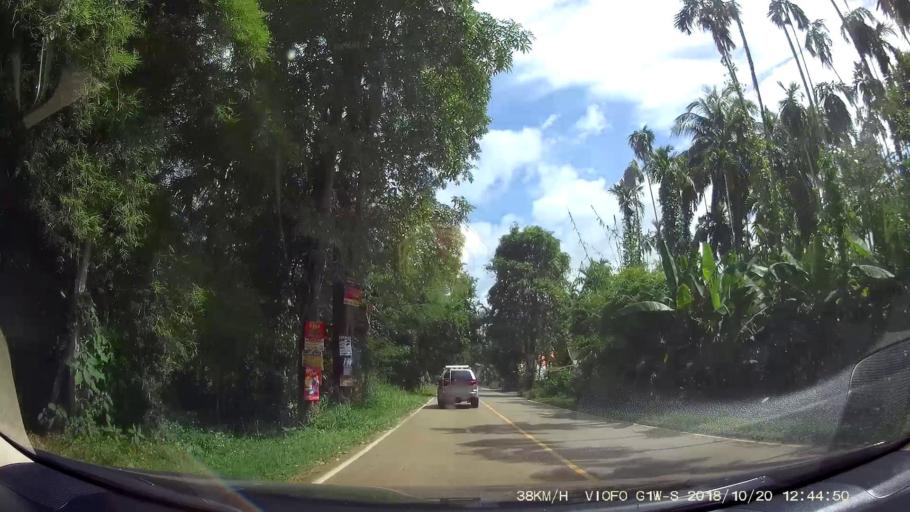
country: TH
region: Chaiyaphum
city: Khon San
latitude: 16.5376
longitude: 101.8717
